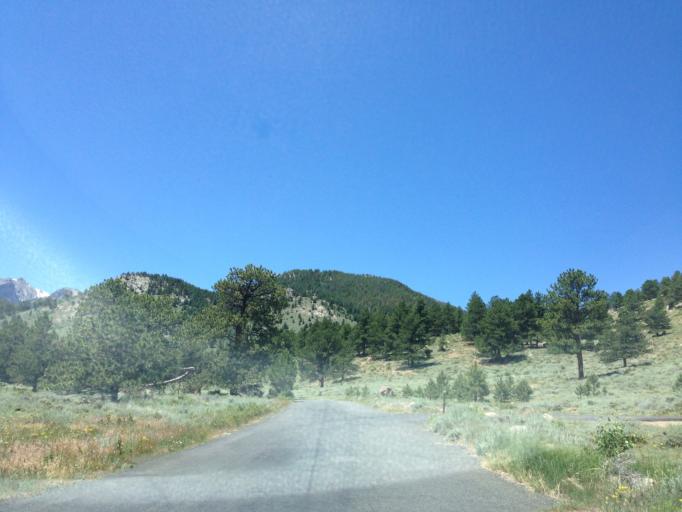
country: US
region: Colorado
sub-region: Larimer County
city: Estes Park
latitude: 40.3424
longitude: -105.6030
